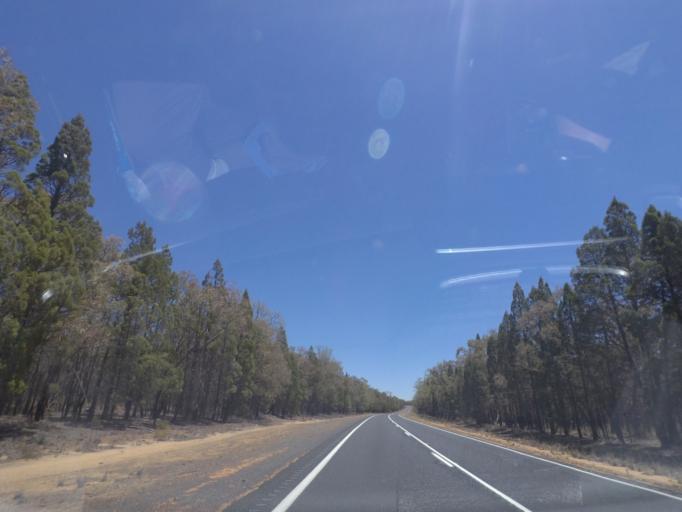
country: AU
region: New South Wales
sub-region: Warrumbungle Shire
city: Coonabarabran
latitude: -31.1989
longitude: 149.3468
